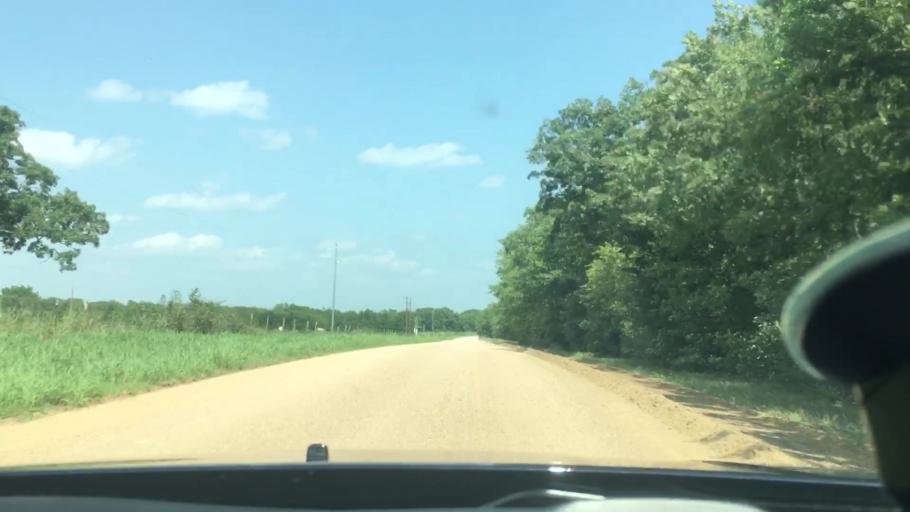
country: US
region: Oklahoma
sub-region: Coal County
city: Coalgate
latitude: 34.4313
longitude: -96.4525
